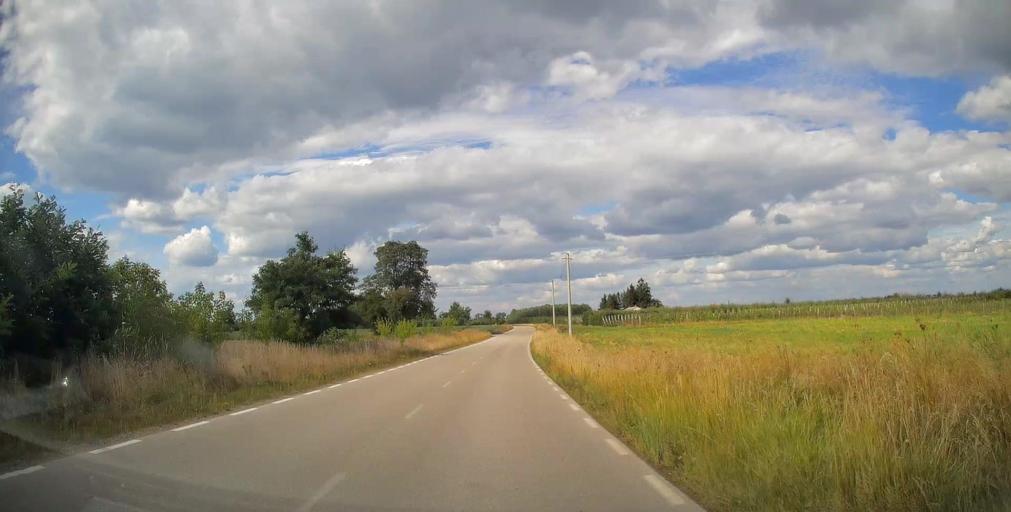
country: PL
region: Masovian Voivodeship
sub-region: Powiat grojecki
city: Goszczyn
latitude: 51.7553
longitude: 20.9023
